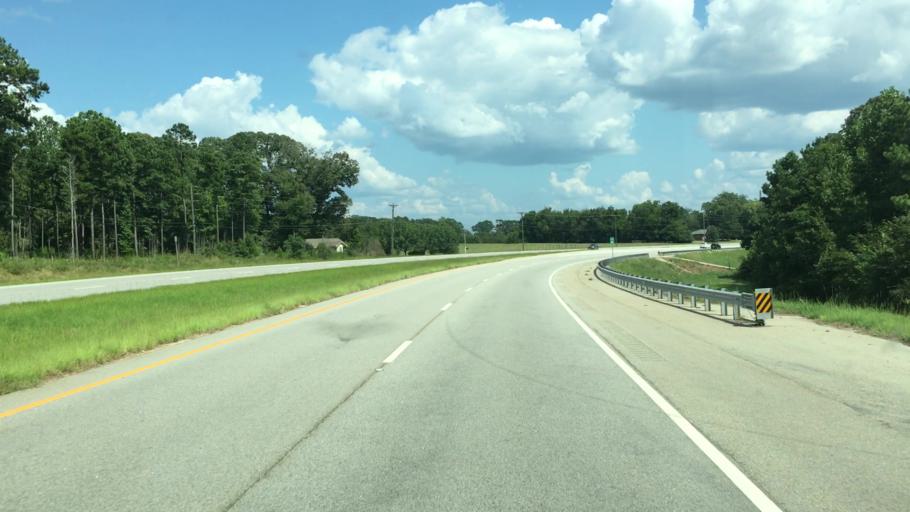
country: US
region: Georgia
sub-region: Putnam County
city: Eatonton
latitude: 33.2695
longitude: -83.3398
